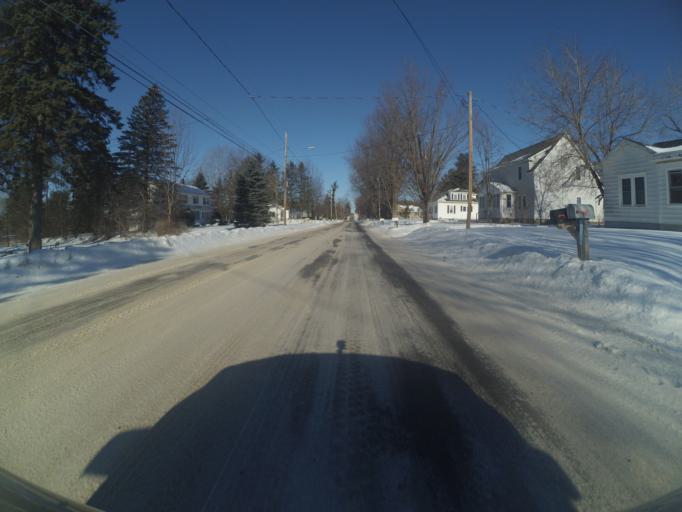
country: US
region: New York
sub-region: St. Lawrence County
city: Potsdam
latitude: 44.6821
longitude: -74.9897
